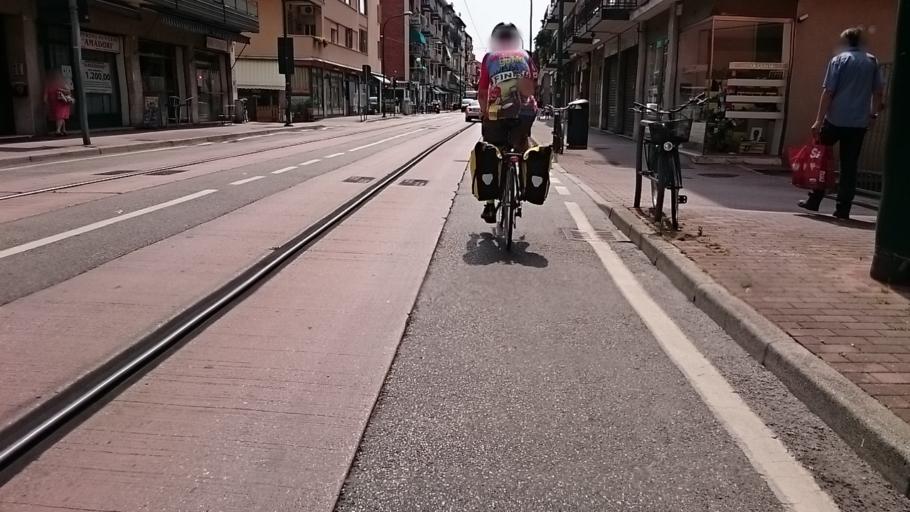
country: IT
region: Veneto
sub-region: Provincia di Venezia
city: Mestre
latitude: 45.4932
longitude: 12.2469
